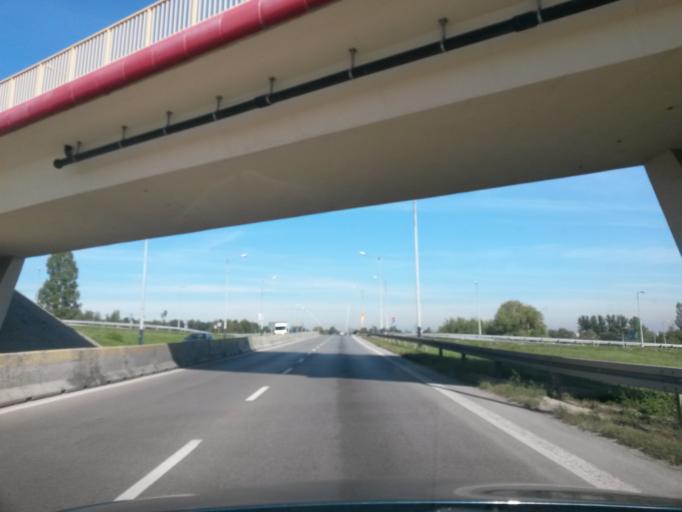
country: PL
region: Lesser Poland Voivodeship
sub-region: Powiat krakowski
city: Libertow
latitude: 49.9908
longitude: 19.9164
